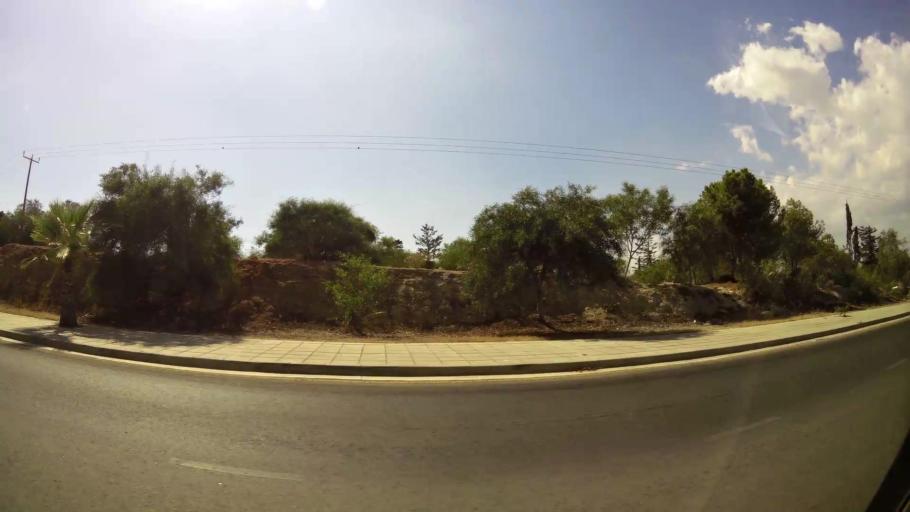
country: CY
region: Larnaka
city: Larnaca
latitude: 34.8908
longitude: 33.6316
